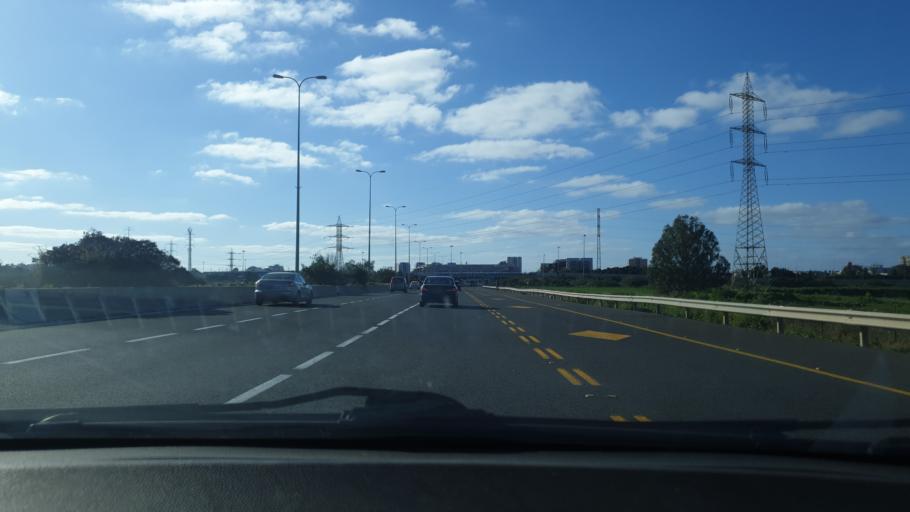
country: IL
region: Tel Aviv
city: Azor
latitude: 32.0361
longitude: 34.7838
